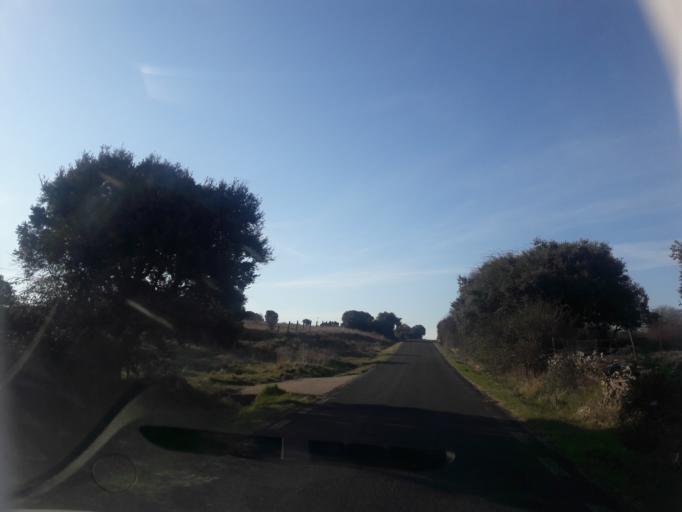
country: ES
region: Castille and Leon
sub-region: Provincia de Salamanca
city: Montejo
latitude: 40.6159
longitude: -5.6072
